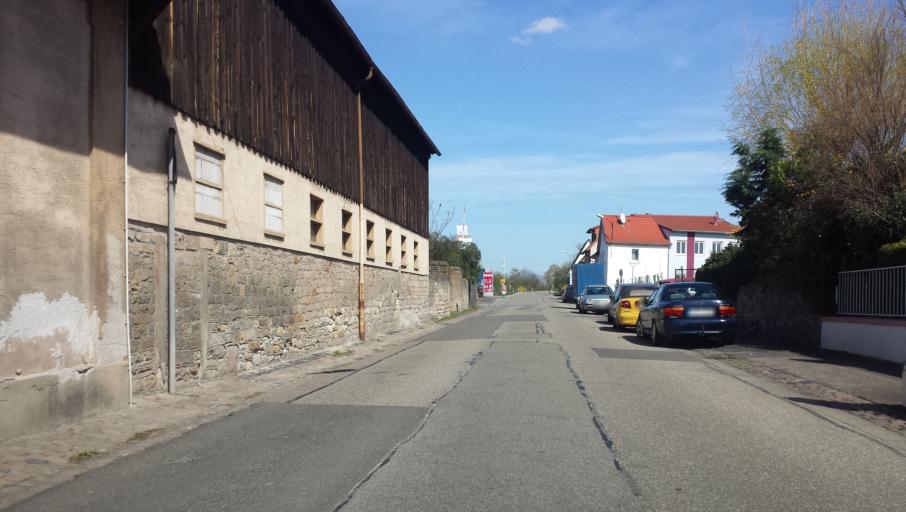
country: DE
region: Rheinland-Pfalz
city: Ruppertsberg
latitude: 49.3698
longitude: 8.1753
